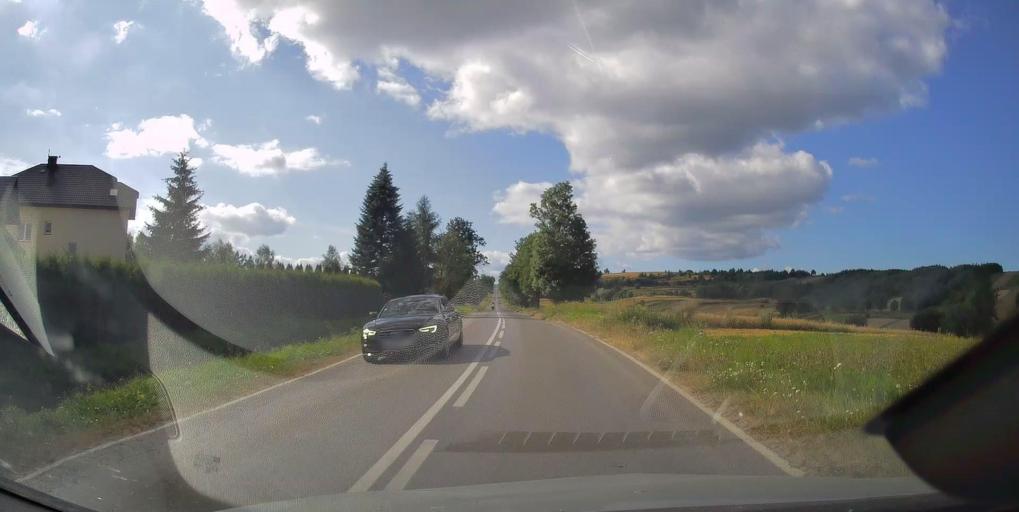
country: PL
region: Swietokrzyskie
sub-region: Powiat skarzyski
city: Suchedniow
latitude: 50.9803
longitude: 20.8775
